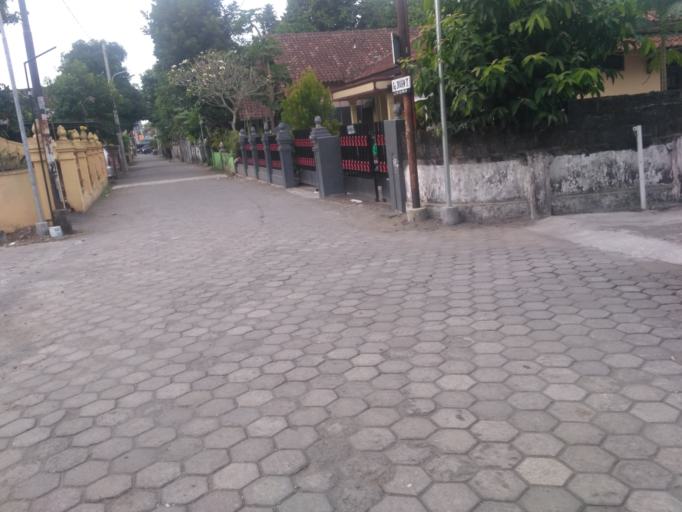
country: ID
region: Daerah Istimewa Yogyakarta
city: Melati
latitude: -7.7521
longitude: 110.3695
